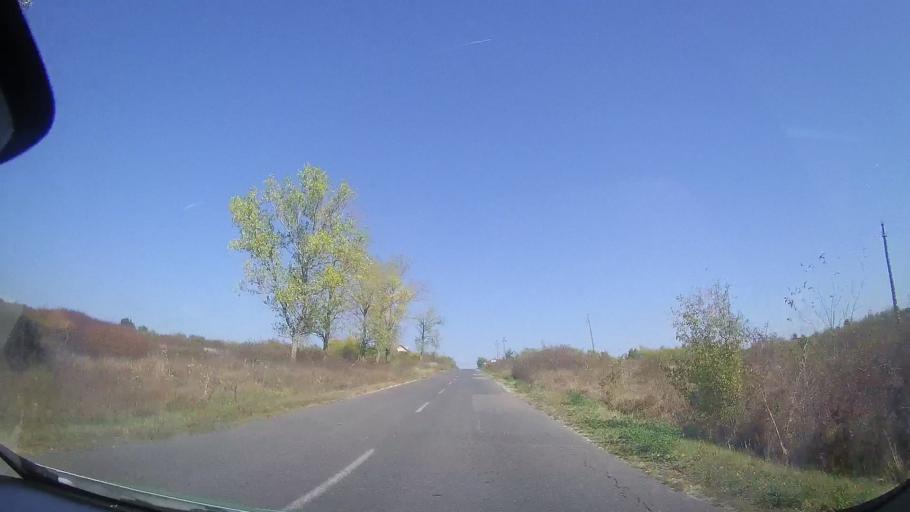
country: RO
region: Timis
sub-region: Comuna Costeiu
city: Costeiu
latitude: 45.7569
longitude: 21.8482
